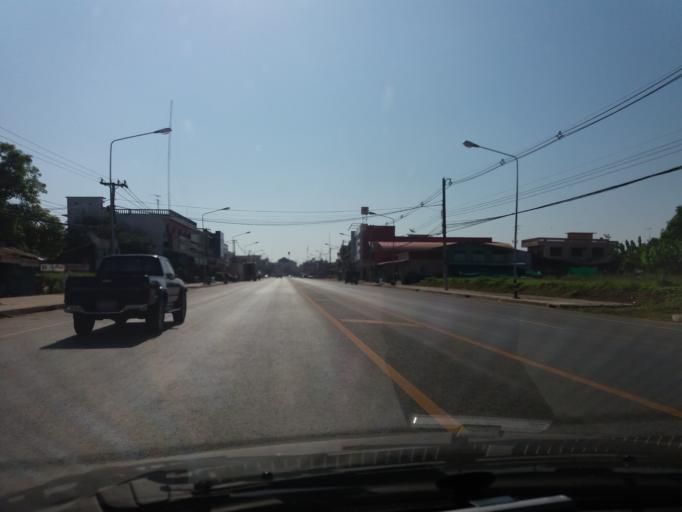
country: TH
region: Kamphaeng Phet
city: Khlong Khlung
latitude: 16.2391
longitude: 99.7285
